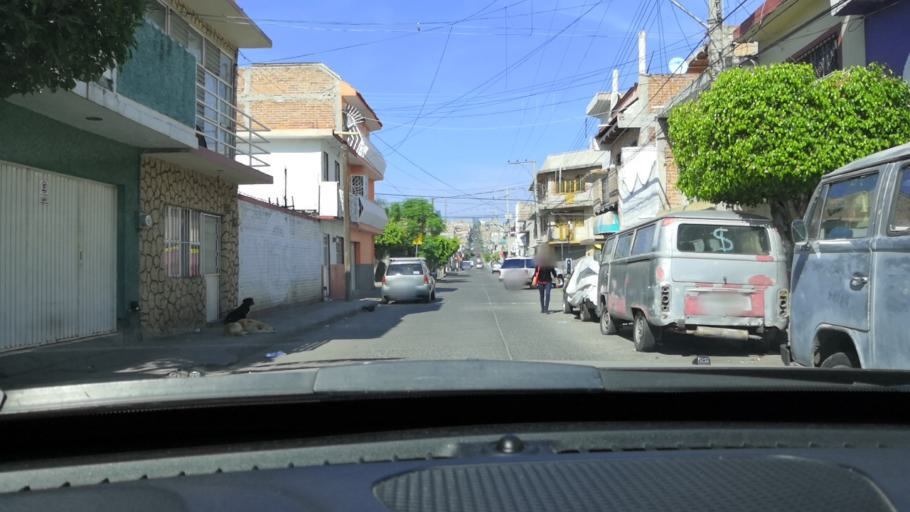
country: MX
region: Guanajuato
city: Leon
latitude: 21.1276
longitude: -101.6968
